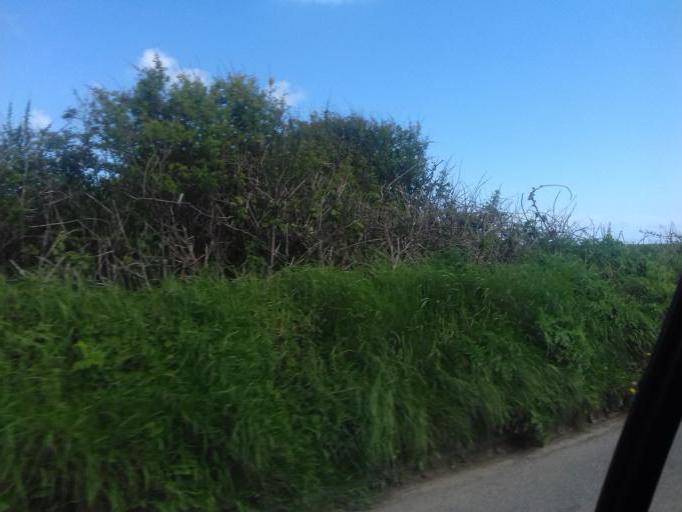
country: IE
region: Munster
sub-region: Waterford
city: Dunmore East
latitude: 52.1918
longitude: -6.8990
